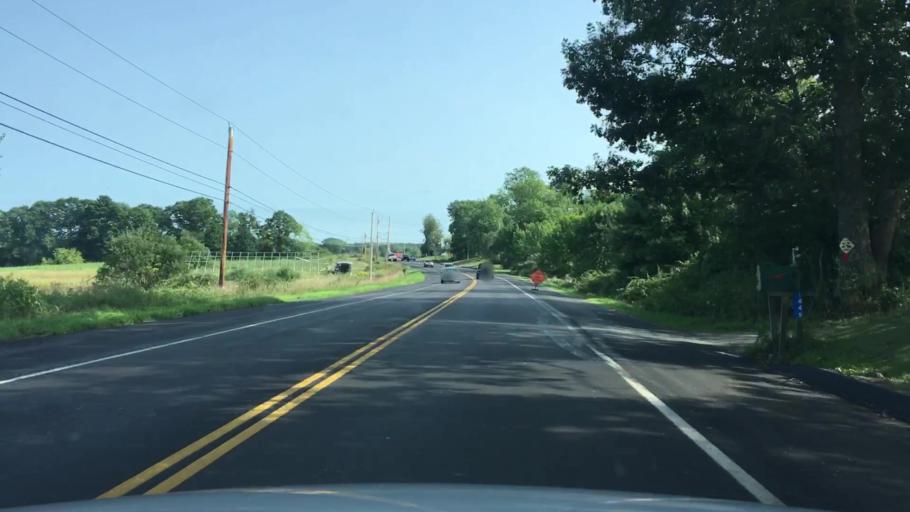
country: US
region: Maine
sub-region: Knox County
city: Warren
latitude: 44.1072
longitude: -69.2523
